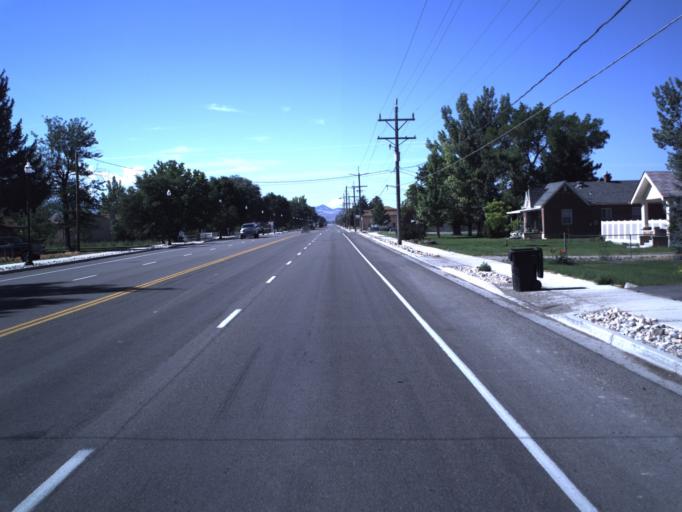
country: US
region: Utah
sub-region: Sanpete County
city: Centerfield
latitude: 39.1282
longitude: -111.8193
